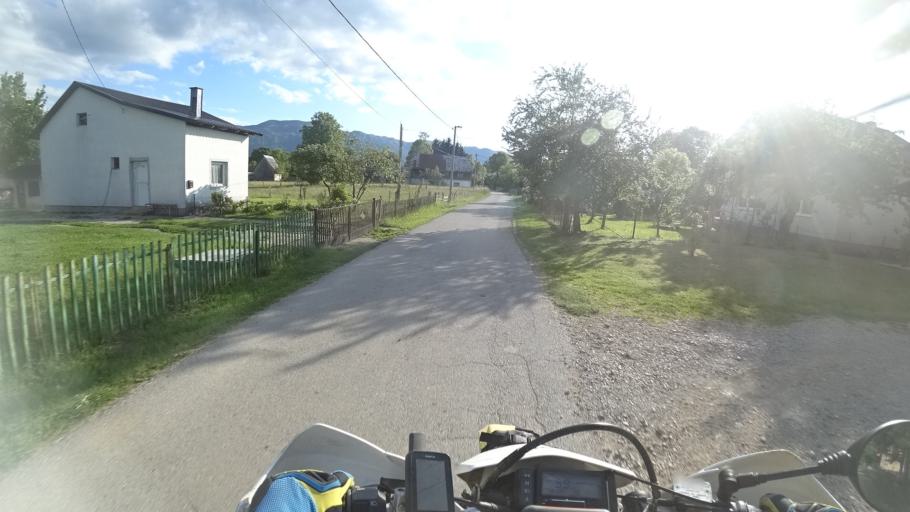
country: HR
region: Licko-Senjska
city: Gospic
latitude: 44.5146
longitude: 15.3280
